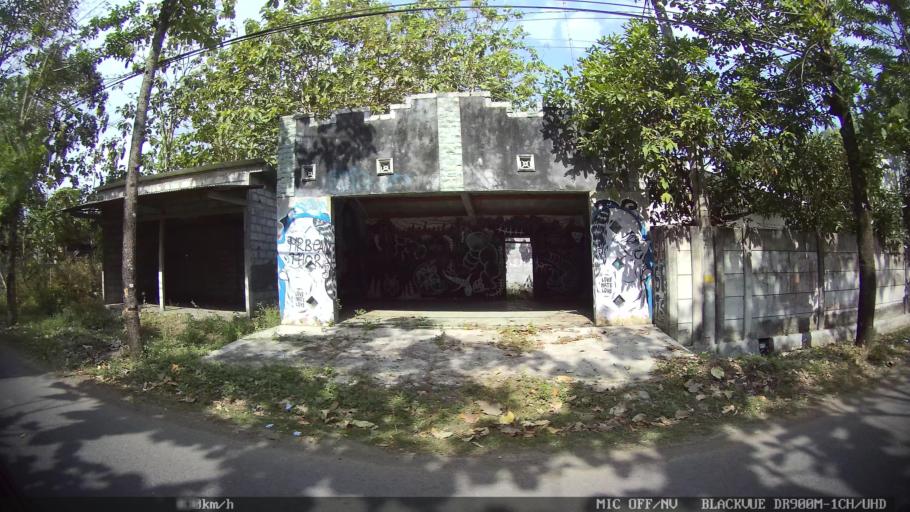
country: ID
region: Daerah Istimewa Yogyakarta
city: Bantul
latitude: -7.8579
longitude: 110.3006
